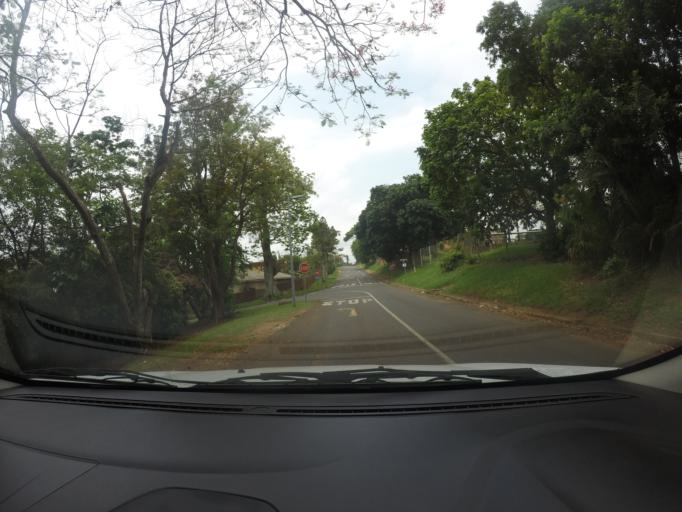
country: ZA
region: KwaZulu-Natal
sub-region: uThungulu District Municipality
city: Empangeni
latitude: -28.7499
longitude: 31.8909
